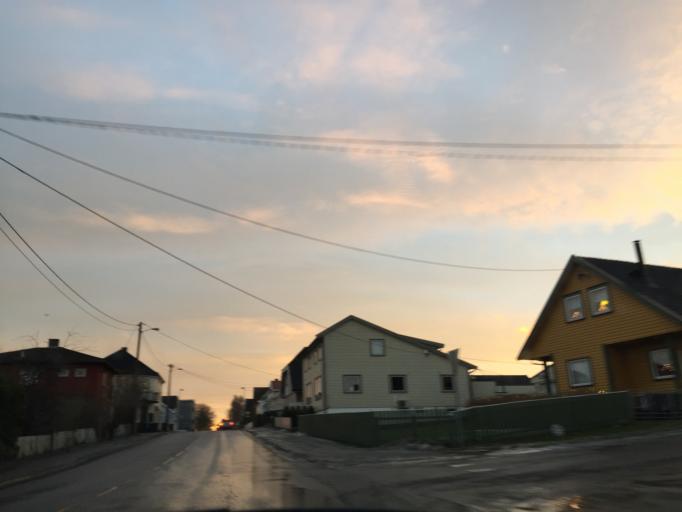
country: NO
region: Ostfold
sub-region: Moss
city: Moss
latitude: 59.4354
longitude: 10.6425
